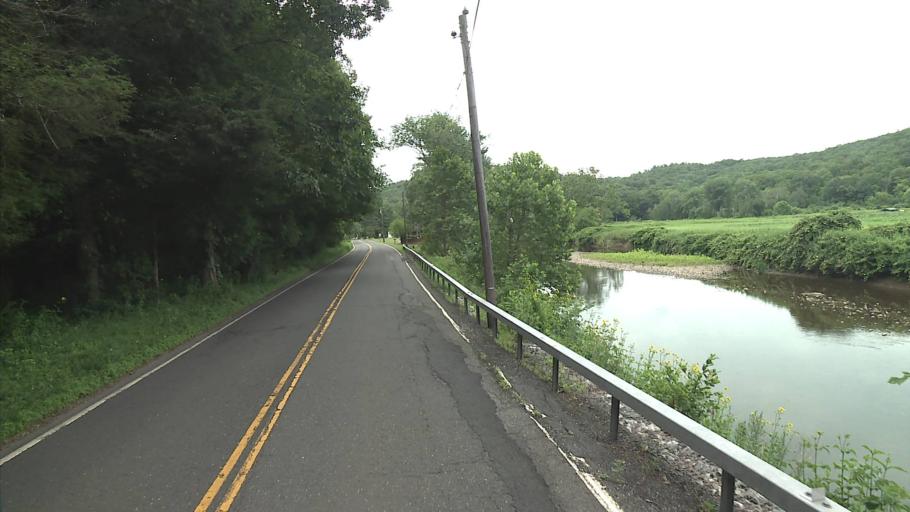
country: US
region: Connecticut
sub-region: Litchfield County
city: New Milford
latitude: 41.5611
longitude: -73.3288
